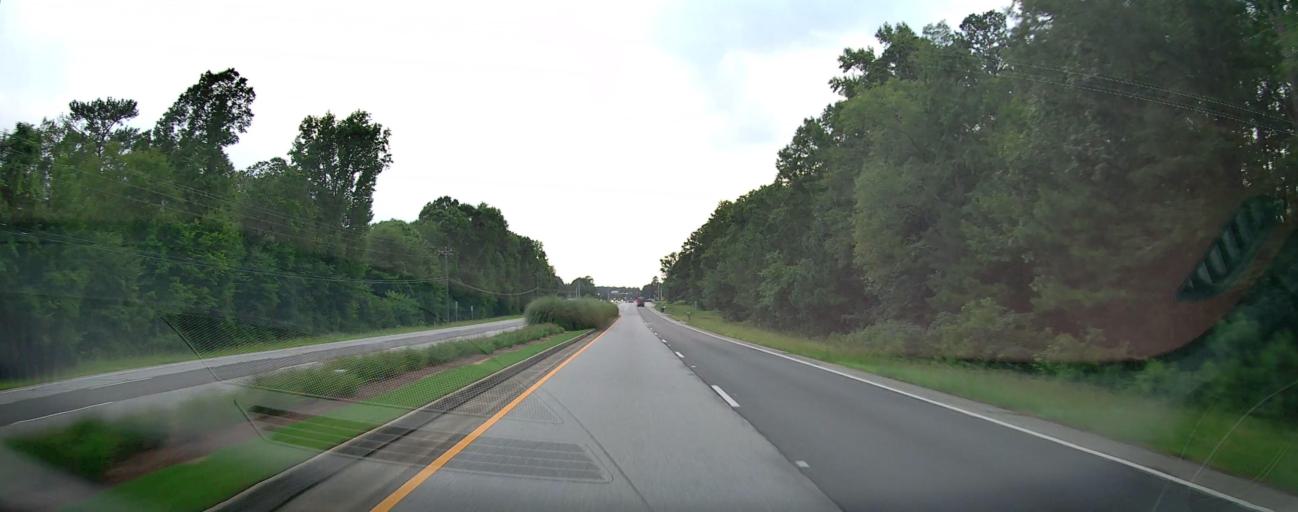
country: US
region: Georgia
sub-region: Muscogee County
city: Columbus
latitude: 32.5394
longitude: -84.8357
